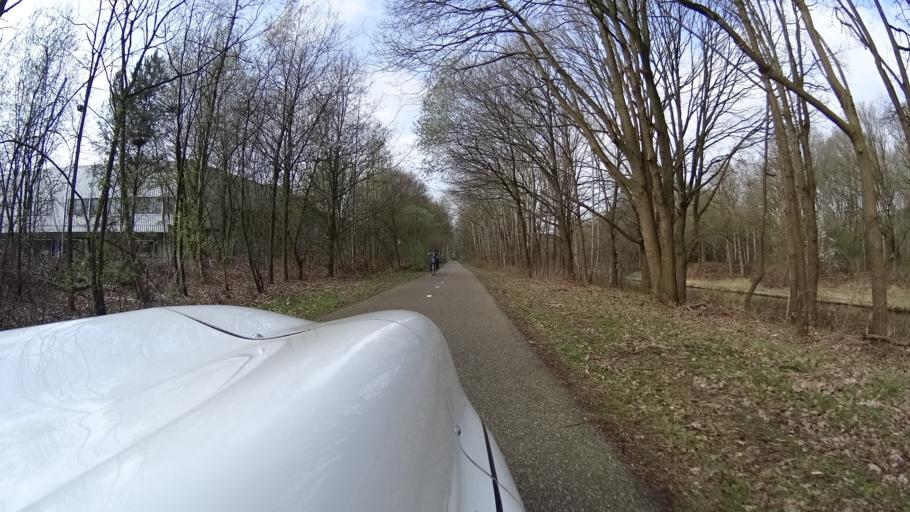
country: NL
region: North Brabant
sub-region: Gemeente Son en Breugel
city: Son
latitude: 51.5040
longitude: 5.4580
